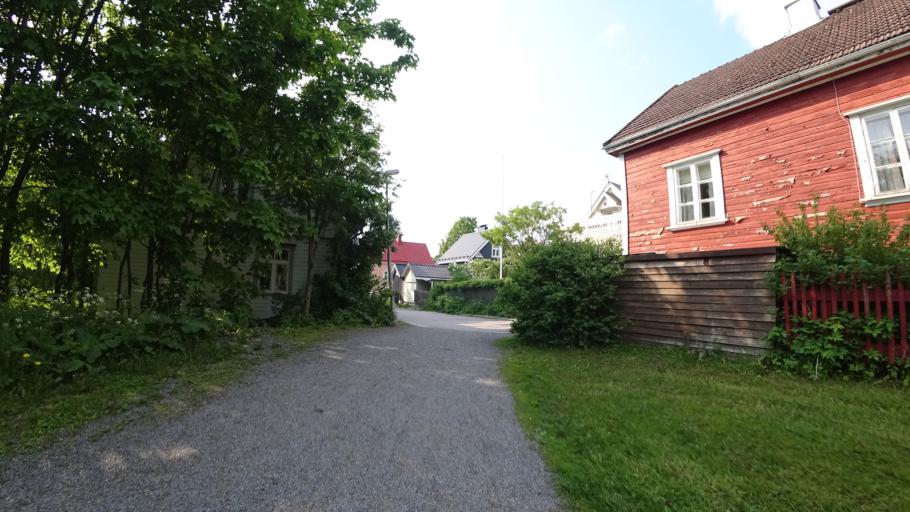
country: FI
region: Pirkanmaa
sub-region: Tampere
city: Pirkkala
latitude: 61.5036
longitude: 23.7017
